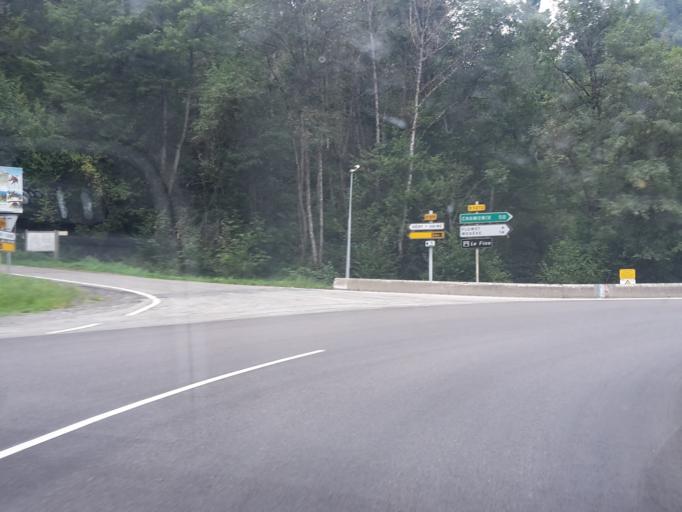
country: FR
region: Rhone-Alpes
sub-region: Departement de la Savoie
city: Ugine
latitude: 45.7946
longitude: 6.4837
